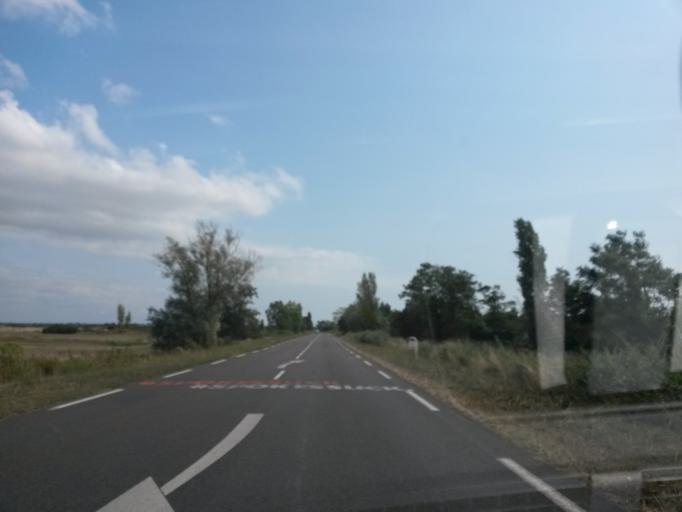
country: FR
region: Pays de la Loire
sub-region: Departement de la Vendee
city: La Tranche-sur-Mer
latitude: 46.3596
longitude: -1.4475
